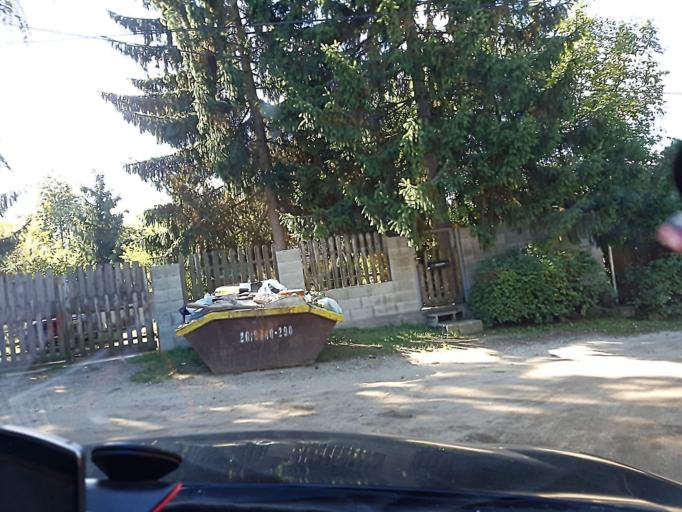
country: HU
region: Pest
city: Piliscsaba
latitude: 47.6342
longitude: 18.8503
